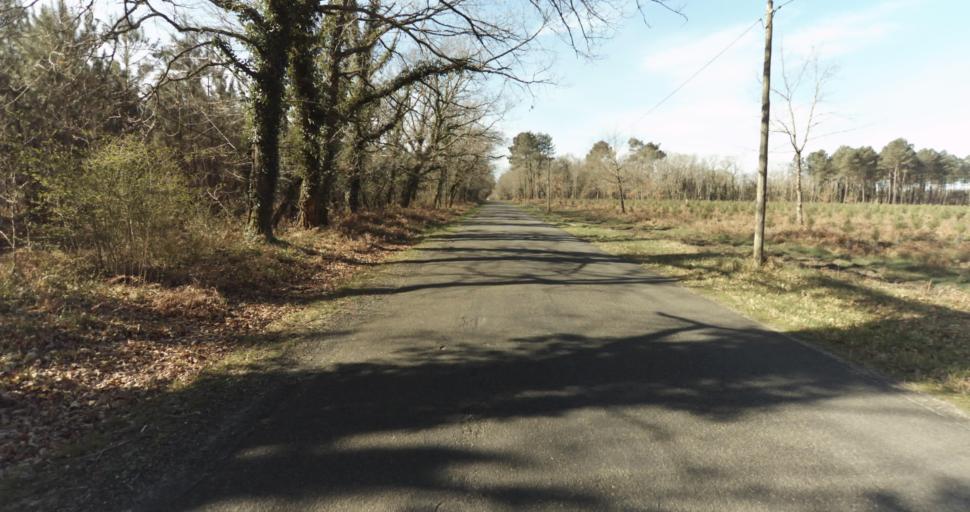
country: FR
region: Aquitaine
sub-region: Departement des Landes
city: Roquefort
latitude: 44.0973
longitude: -0.2968
